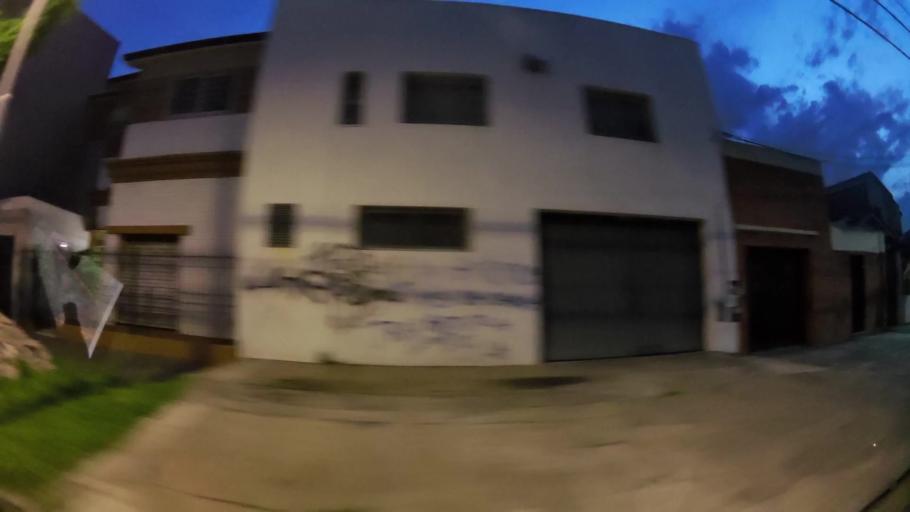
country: AR
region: Buenos Aires
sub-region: Partido de Avellaneda
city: Avellaneda
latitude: -34.6968
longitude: -58.3199
